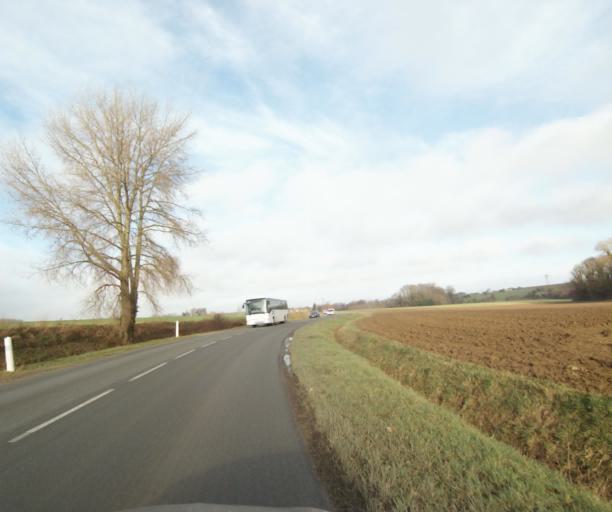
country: FR
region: Nord-Pas-de-Calais
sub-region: Departement du Nord
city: Thiant
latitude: 50.2730
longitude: 3.4546
